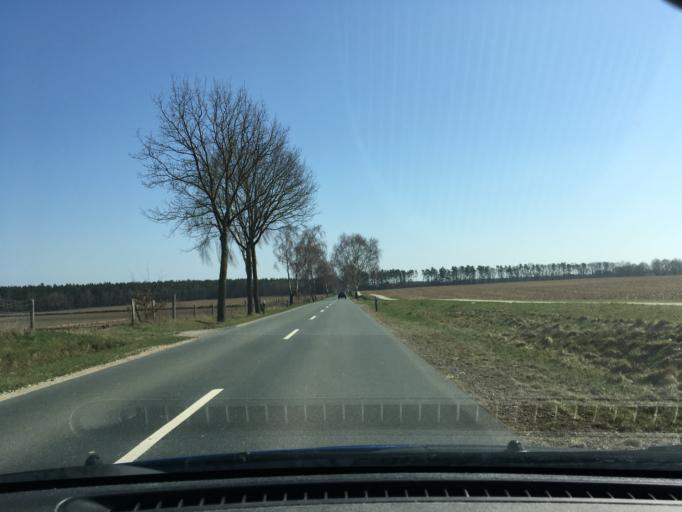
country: DE
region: Lower Saxony
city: Wriedel
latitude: 53.0034
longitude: 10.2937
